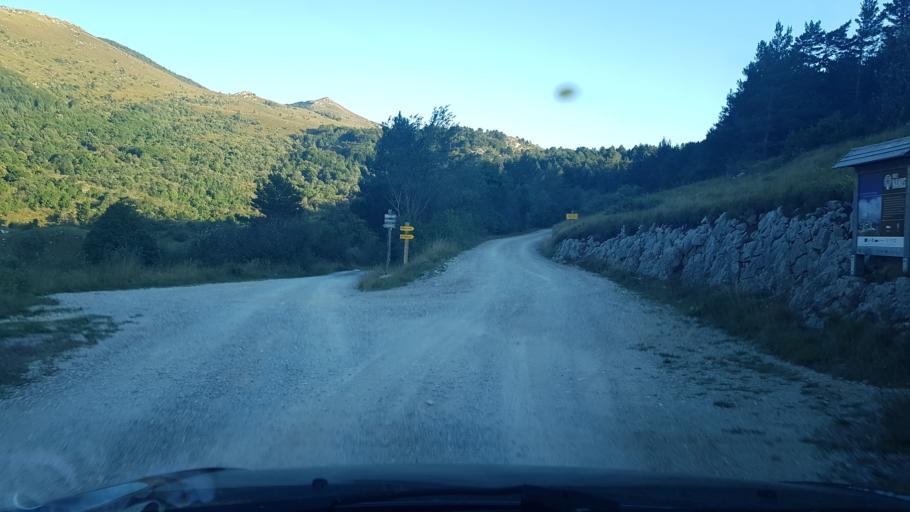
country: SI
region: Vipava
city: Vipava
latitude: 45.7930
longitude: 14.0196
